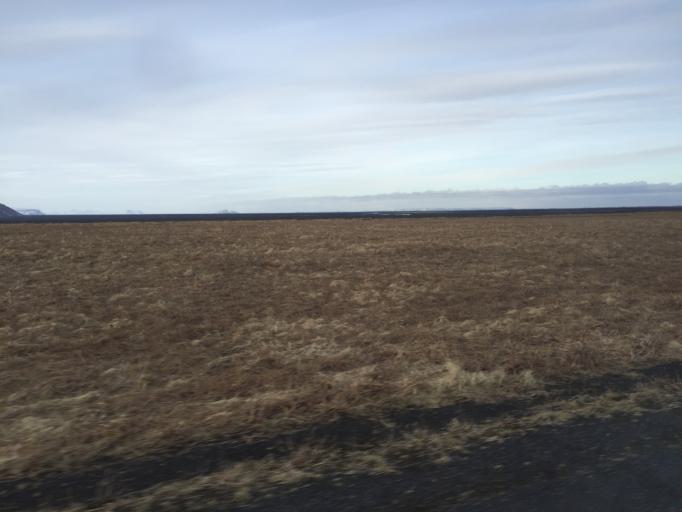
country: IS
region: South
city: Vestmannaeyjar
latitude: 63.4460
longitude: -18.6985
